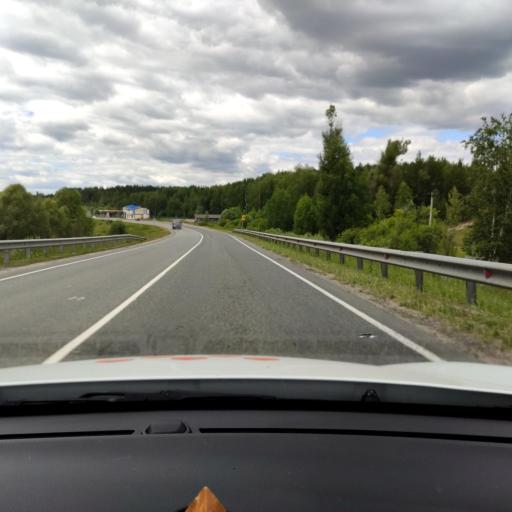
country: RU
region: Tatarstan
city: Aysha
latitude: 55.8785
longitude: 48.6563
